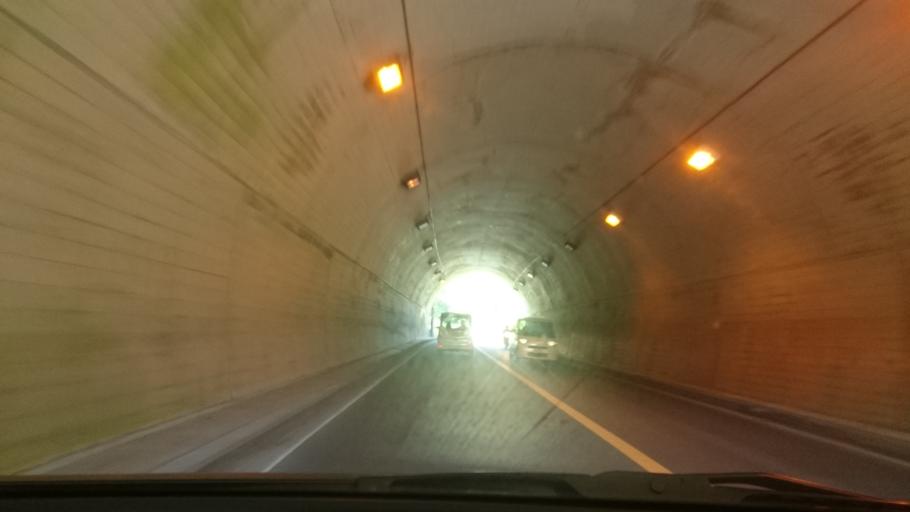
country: JP
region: Shizuoka
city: Heda
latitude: 34.7936
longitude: 138.7642
